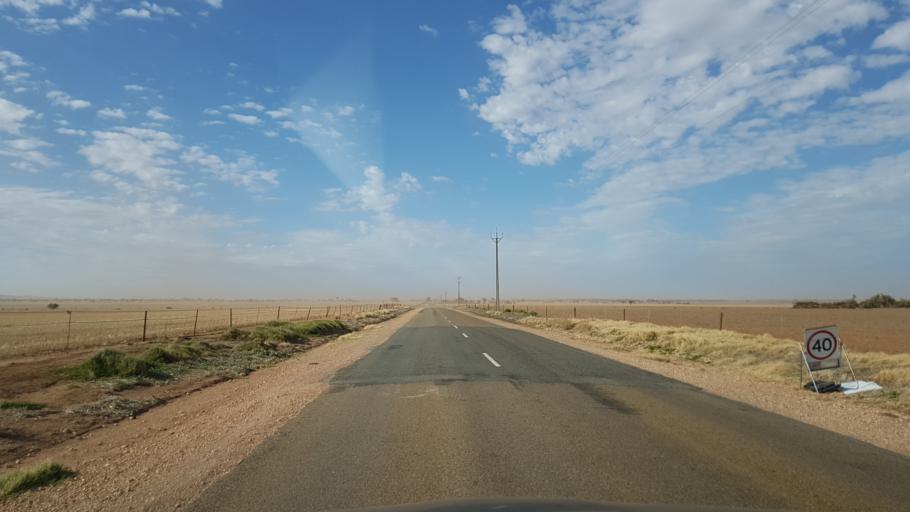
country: AU
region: South Australia
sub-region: Clare and Gilbert Valleys
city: Clare
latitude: -33.8862
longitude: 138.4805
